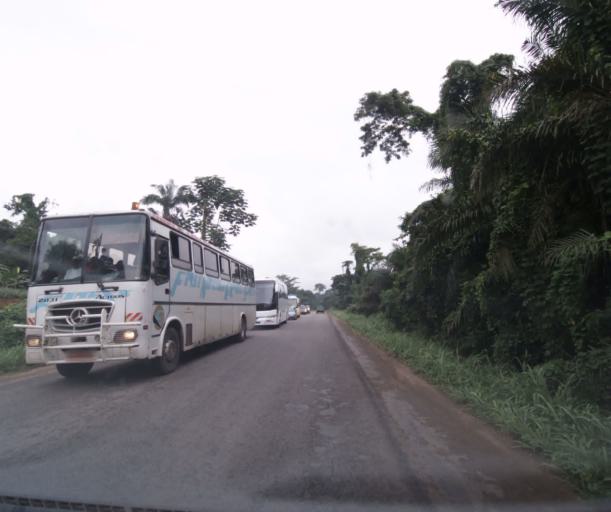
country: CM
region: Centre
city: Eseka
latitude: 3.8499
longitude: 10.4881
